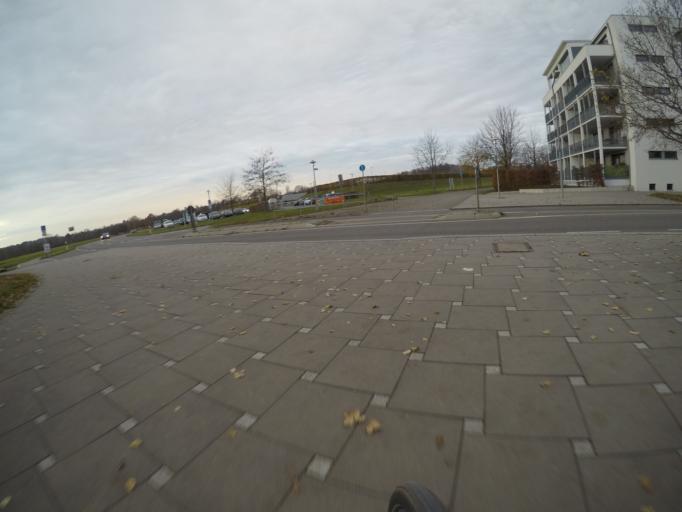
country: DE
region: Baden-Wuerttemberg
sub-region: Regierungsbezirk Stuttgart
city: Ostfildern
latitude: 48.7209
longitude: 9.2657
